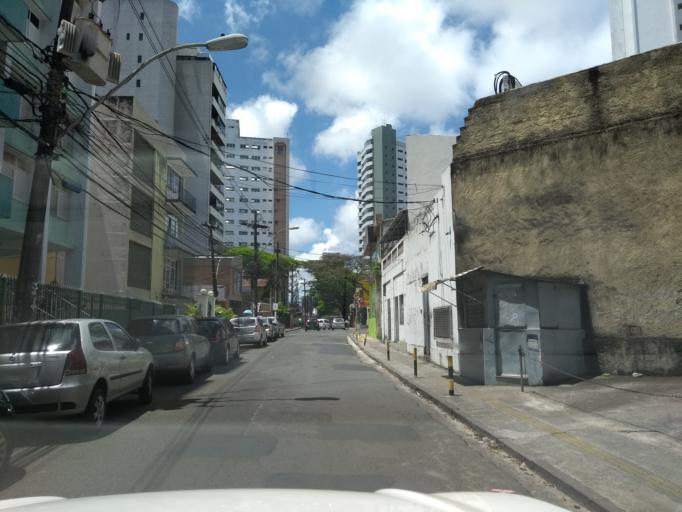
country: BR
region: Bahia
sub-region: Salvador
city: Salvador
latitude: -12.9984
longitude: -38.5228
